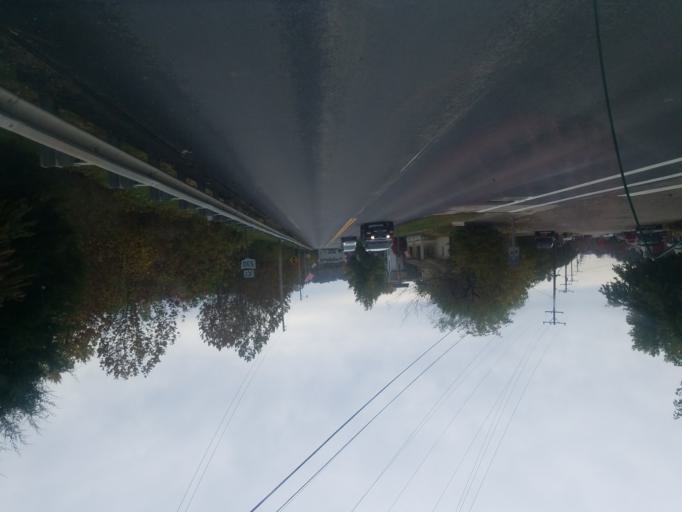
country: US
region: Ohio
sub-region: Washington County
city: Devola
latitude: 39.5303
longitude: -81.5087
